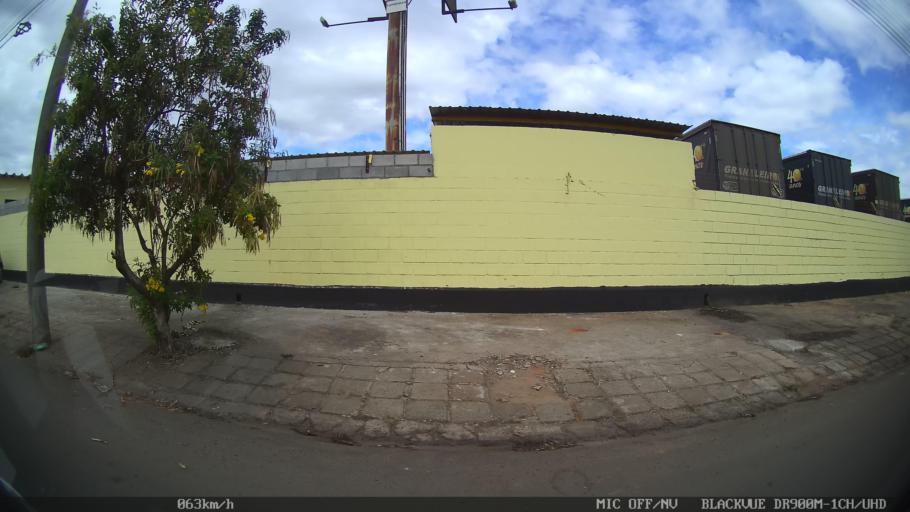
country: BR
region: Sao Paulo
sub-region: Sao Jose Do Rio Preto
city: Sao Jose do Rio Preto
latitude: -20.8109
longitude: -49.4939
